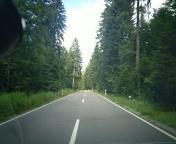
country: DE
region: Baden-Wuerttemberg
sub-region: Karlsruhe Region
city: Freudenstadt
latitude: 48.4455
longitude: 8.4002
